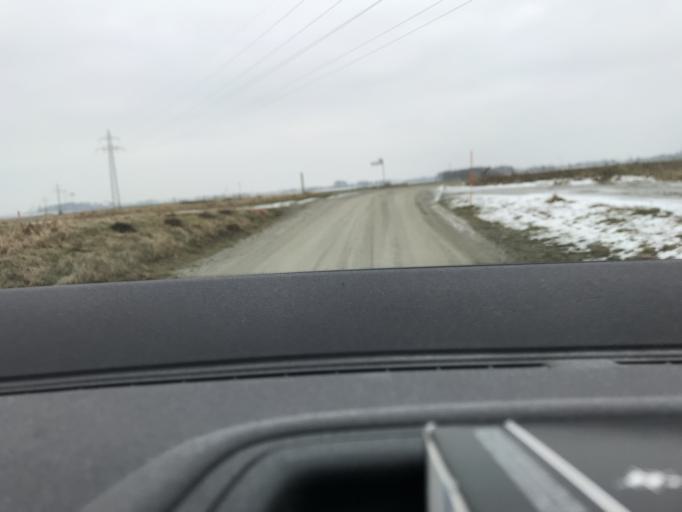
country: SE
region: Skane
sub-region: Ystads Kommun
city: Kopingebro
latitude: 55.4603
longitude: 13.8946
